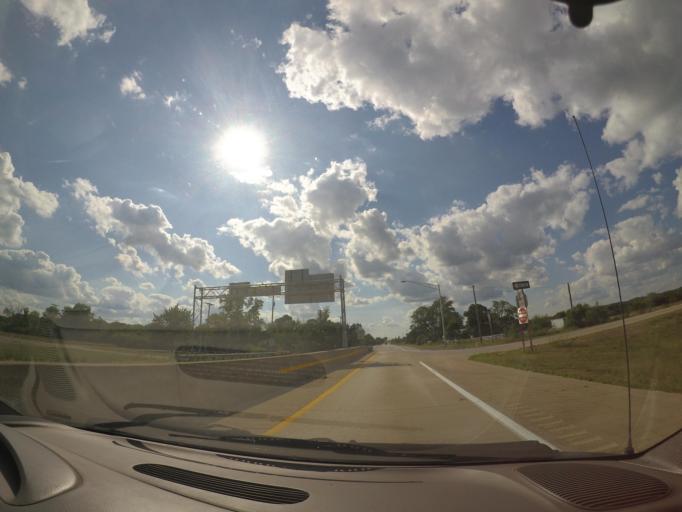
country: US
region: Ohio
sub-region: Wood County
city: Luckey
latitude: 41.4921
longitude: -83.4646
